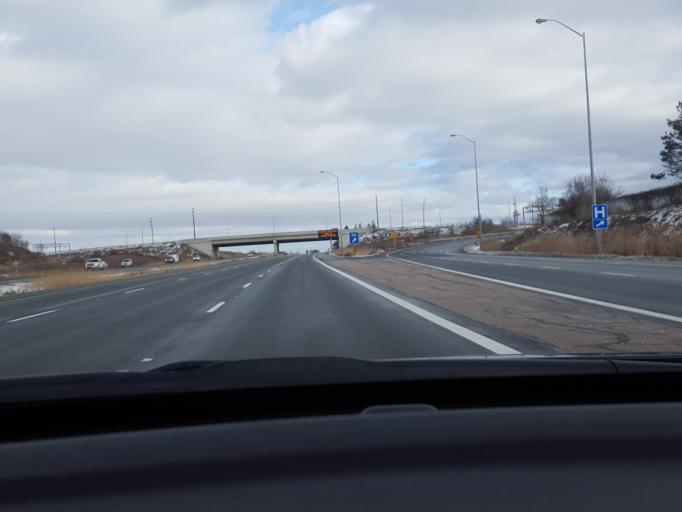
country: CA
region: Ontario
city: Markham
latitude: 43.8690
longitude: -79.2391
